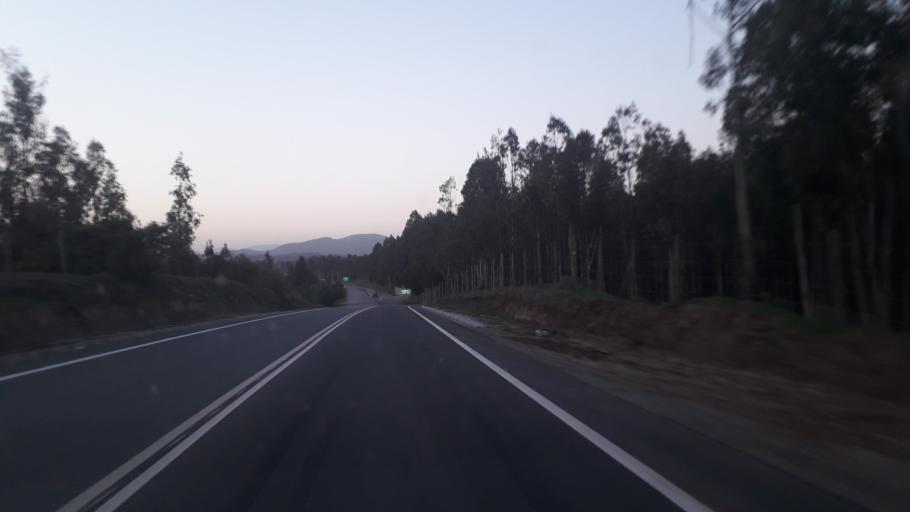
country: CL
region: Valparaiso
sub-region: Provincia de Quillota
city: Hacienda La Calera
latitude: -32.7486
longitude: -71.4186
